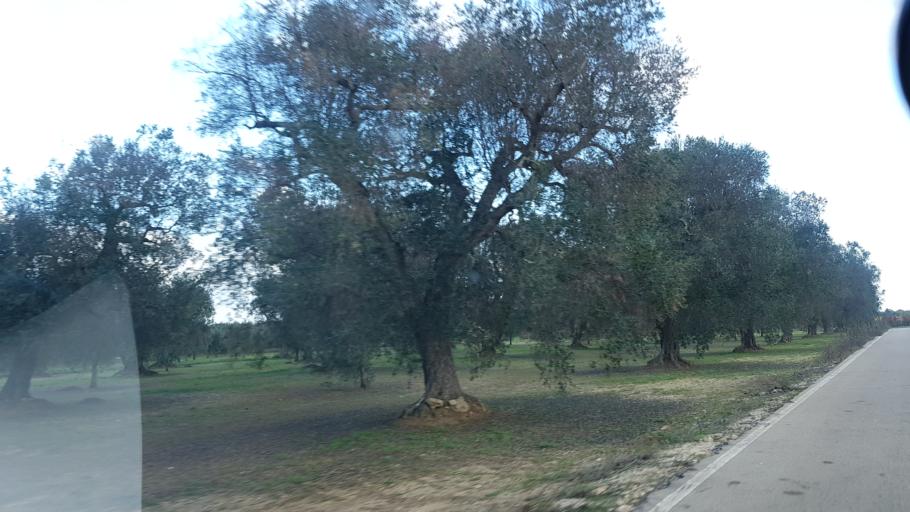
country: IT
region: Apulia
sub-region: Provincia di Brindisi
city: San Pietro Vernotico
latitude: 40.5100
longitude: 18.0200
